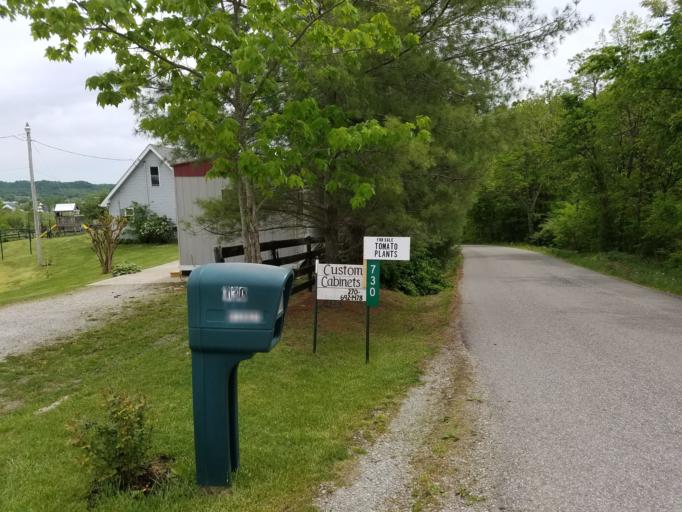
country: US
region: Kentucky
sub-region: Marion County
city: Lebanon
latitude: 37.5754
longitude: -85.0634
